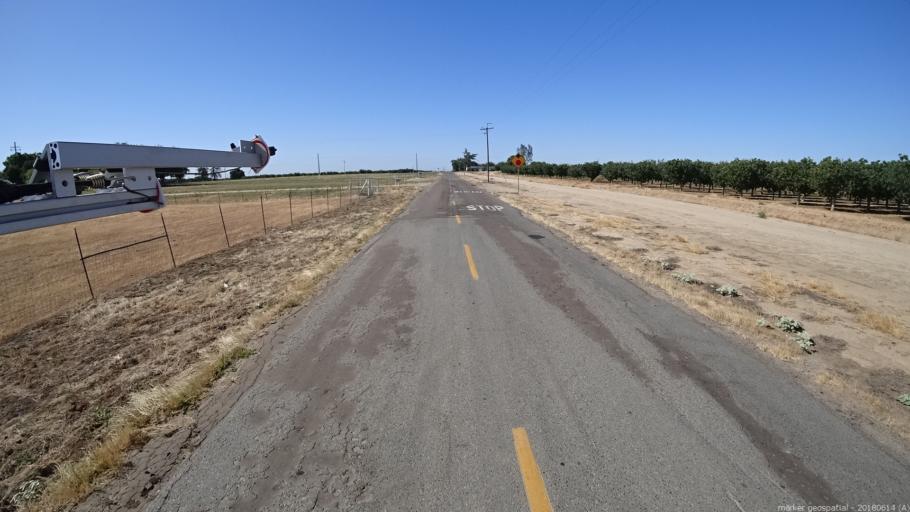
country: US
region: California
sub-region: Madera County
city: Fairmead
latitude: 37.0206
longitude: -120.1661
